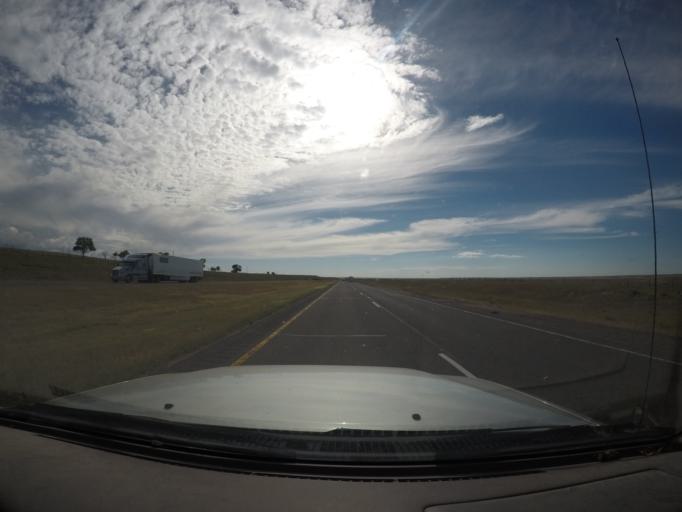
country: US
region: Wyoming
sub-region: Laramie County
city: Pine Bluffs
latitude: 41.1920
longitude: -103.9379
